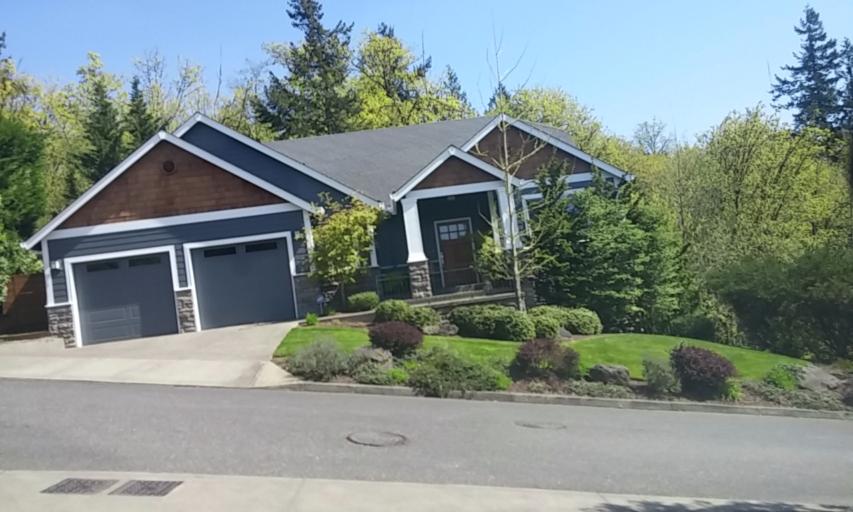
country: US
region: Oregon
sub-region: Washington County
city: West Haven
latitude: 45.5349
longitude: -122.7632
